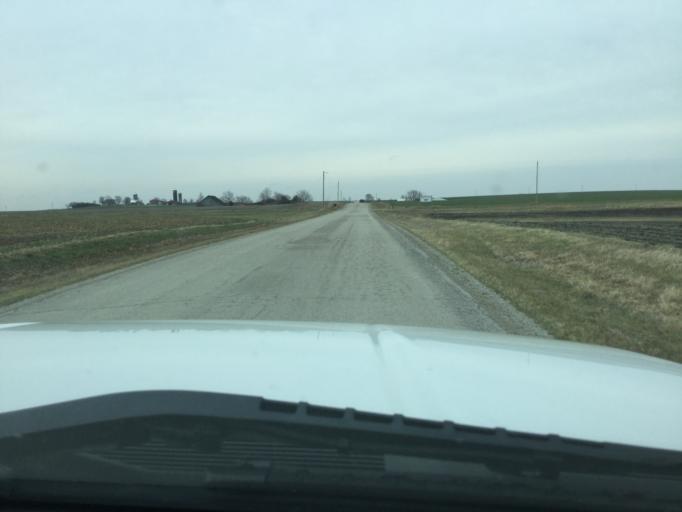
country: US
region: Kansas
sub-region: Nemaha County
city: Sabetha
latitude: 39.8992
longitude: -95.7060
